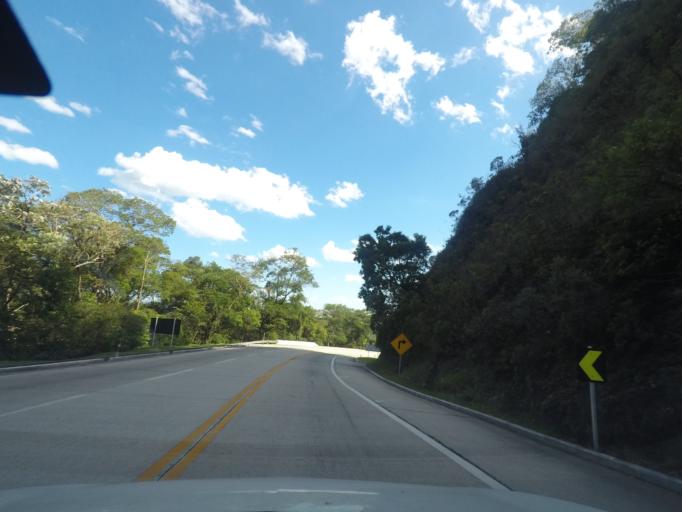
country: BR
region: Rio de Janeiro
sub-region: Guapimirim
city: Guapimirim
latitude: -22.4876
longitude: -42.9976
